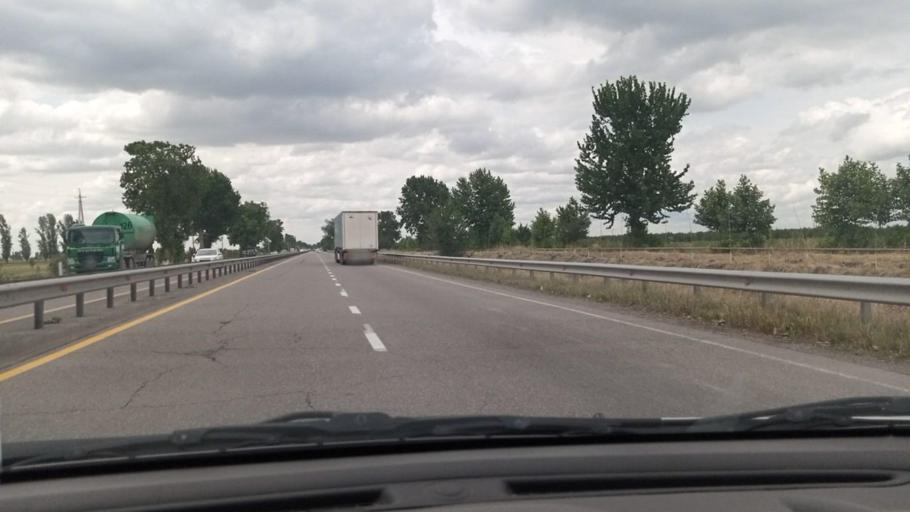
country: UZ
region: Toshkent Shahri
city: Bektemir
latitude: 41.1651
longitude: 69.4178
